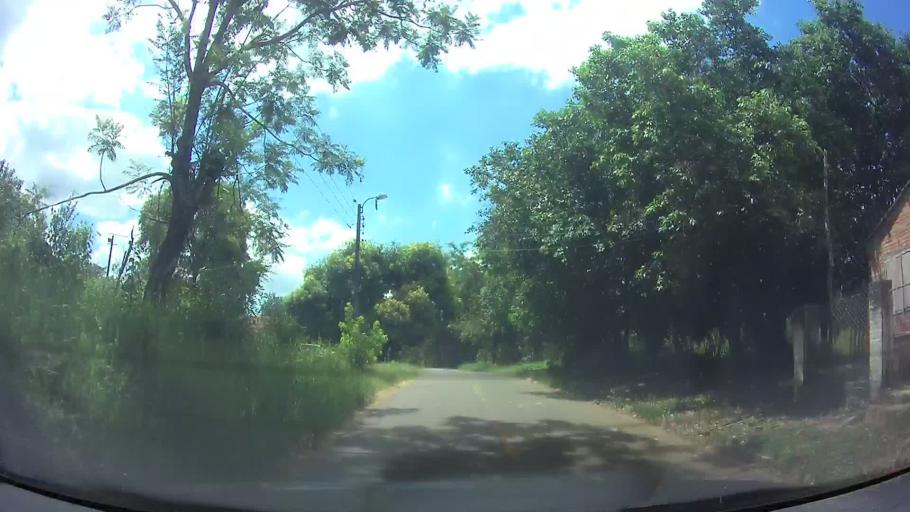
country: PY
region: Central
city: Aregua
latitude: -25.2884
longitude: -57.4117
